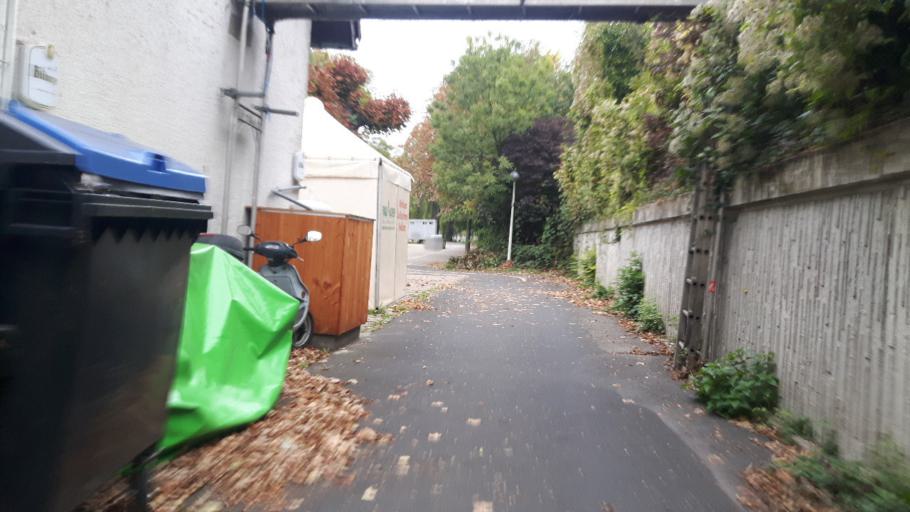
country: DE
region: North Rhine-Westphalia
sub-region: Regierungsbezirk Koln
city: Konigswinter
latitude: 50.7083
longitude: 7.1675
